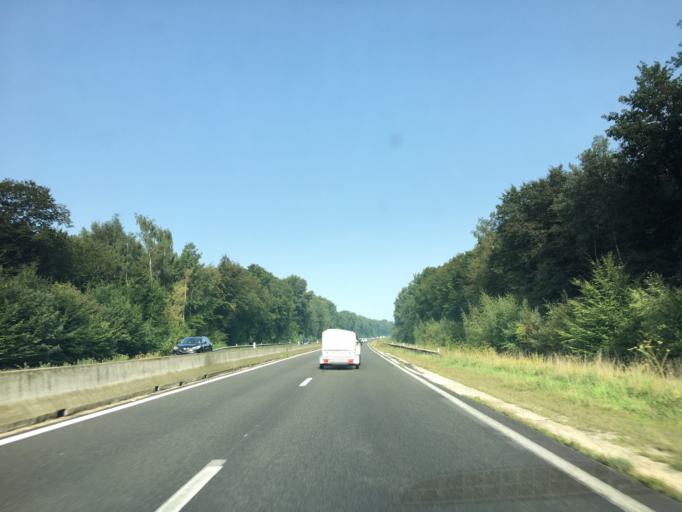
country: FR
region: Ile-de-France
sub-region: Departement de Seine-et-Marne
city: Ozoir-la-Ferriere
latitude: 48.7407
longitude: 2.6939
